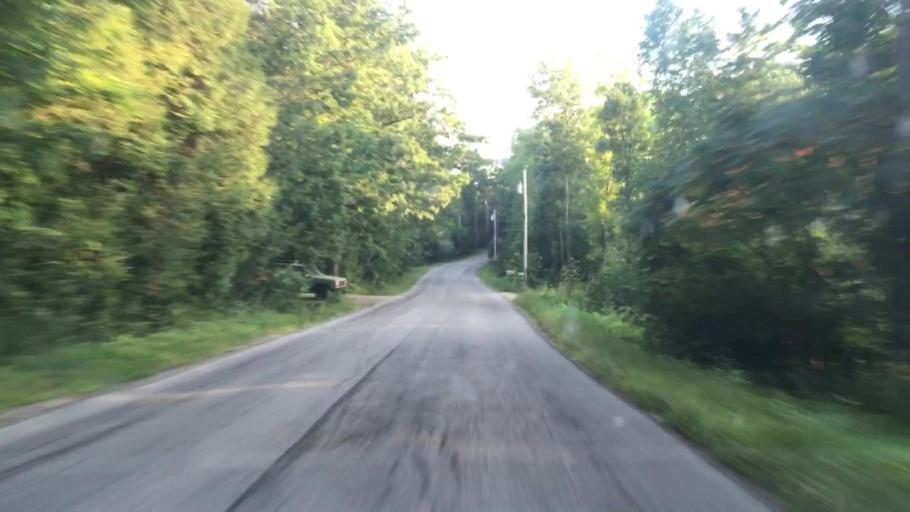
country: US
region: Maine
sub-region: Waldo County
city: Frankfort
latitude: 44.6668
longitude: -68.9261
